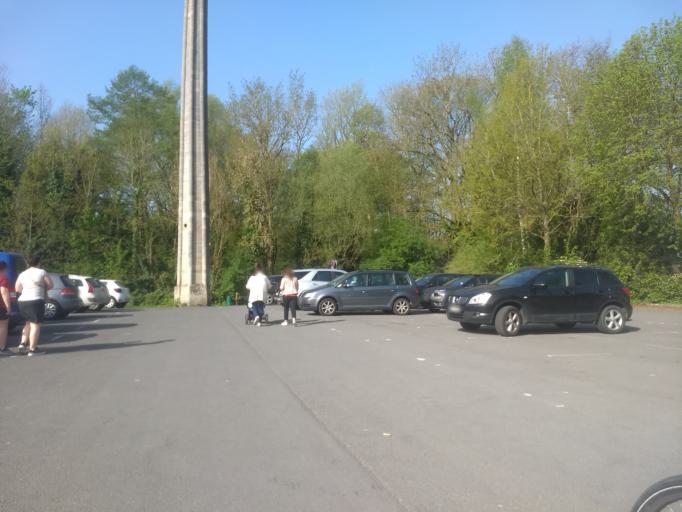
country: FR
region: Nord-Pas-de-Calais
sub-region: Departement du Pas-de-Calais
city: Sainte-Catherine
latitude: 50.3003
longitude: 2.7643
